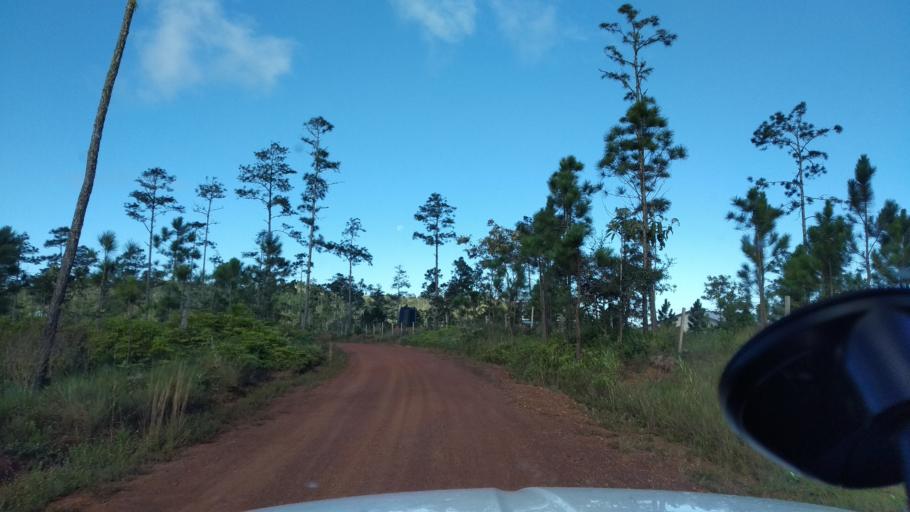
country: BZ
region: Cayo
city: Belmopan
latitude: 16.9985
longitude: -88.8398
